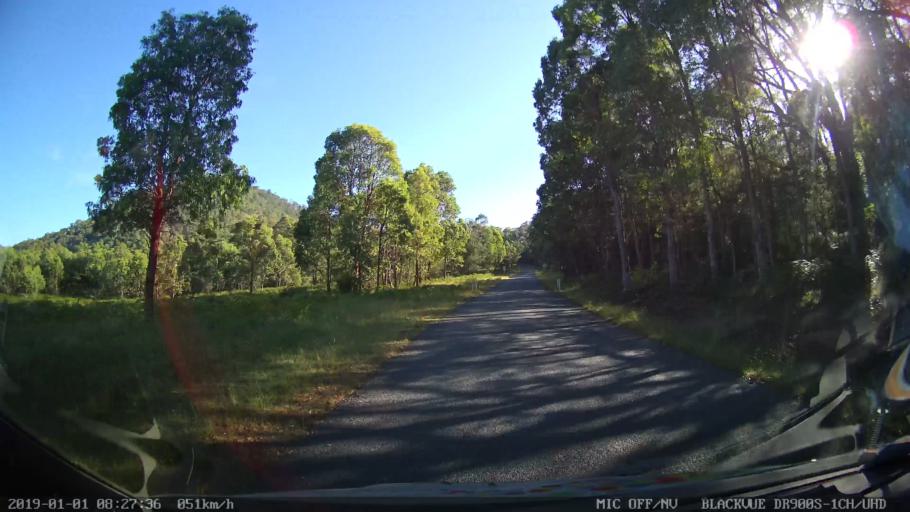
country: AU
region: New South Wales
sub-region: Snowy River
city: Jindabyne
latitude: -36.3804
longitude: 148.1845
